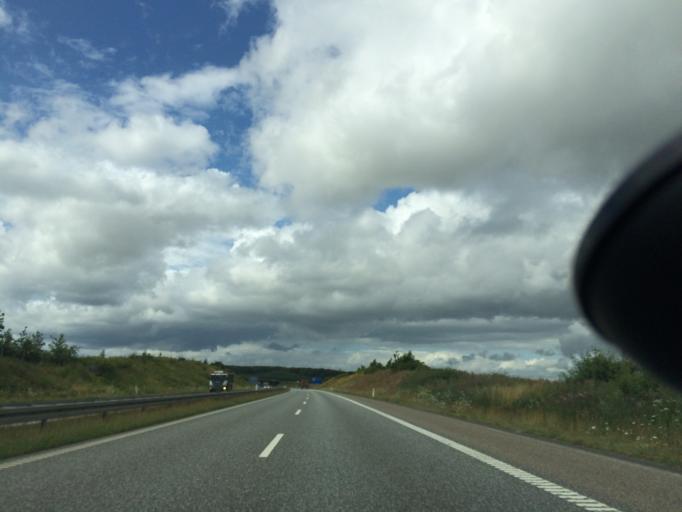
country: DK
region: Central Jutland
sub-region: Arhus Kommune
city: Framlev
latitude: 56.1524
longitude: 9.9874
